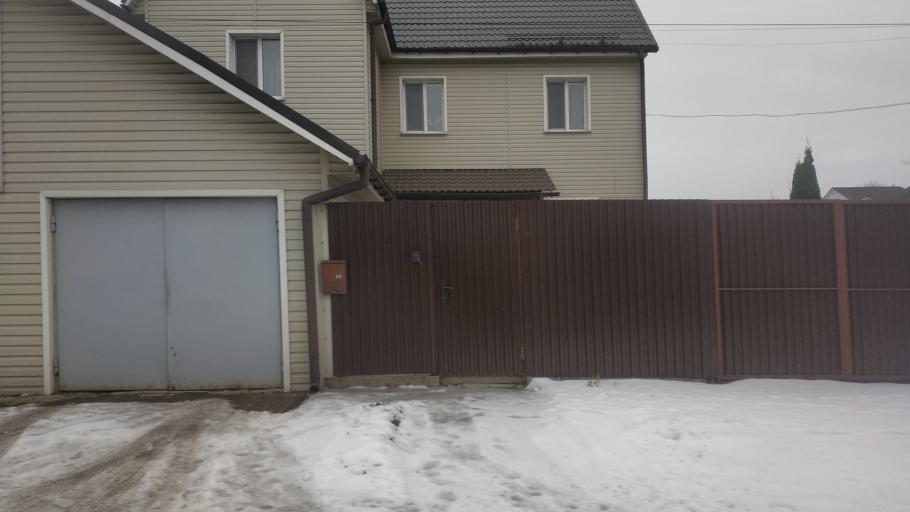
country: RU
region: Tverskaya
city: Tver
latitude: 56.8820
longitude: 35.8845
